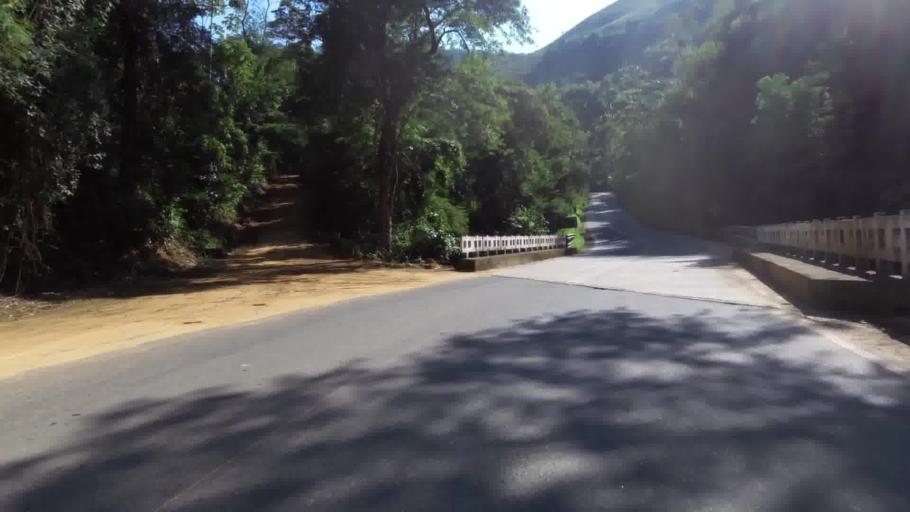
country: BR
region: Espirito Santo
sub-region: Alfredo Chaves
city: Alfredo Chaves
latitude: -20.6036
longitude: -40.7923
